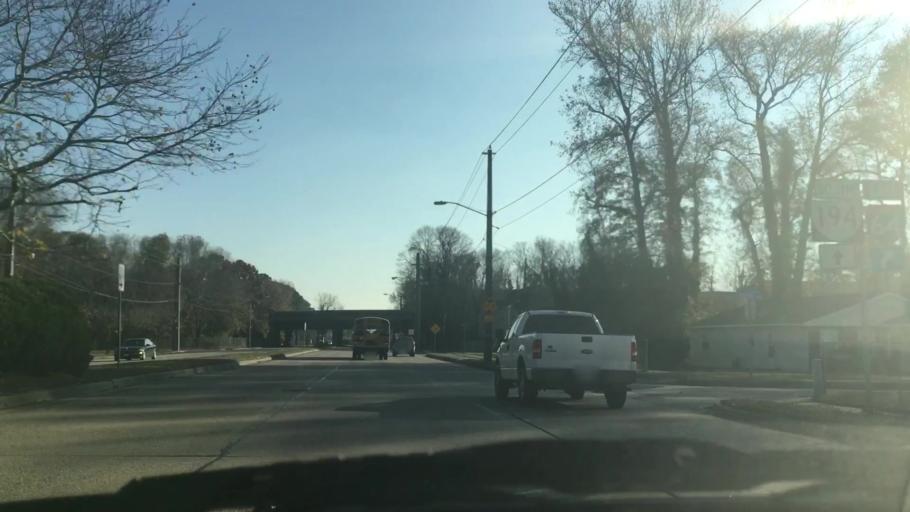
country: US
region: Virginia
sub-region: City of Norfolk
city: Norfolk
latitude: 36.9051
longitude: -76.2400
